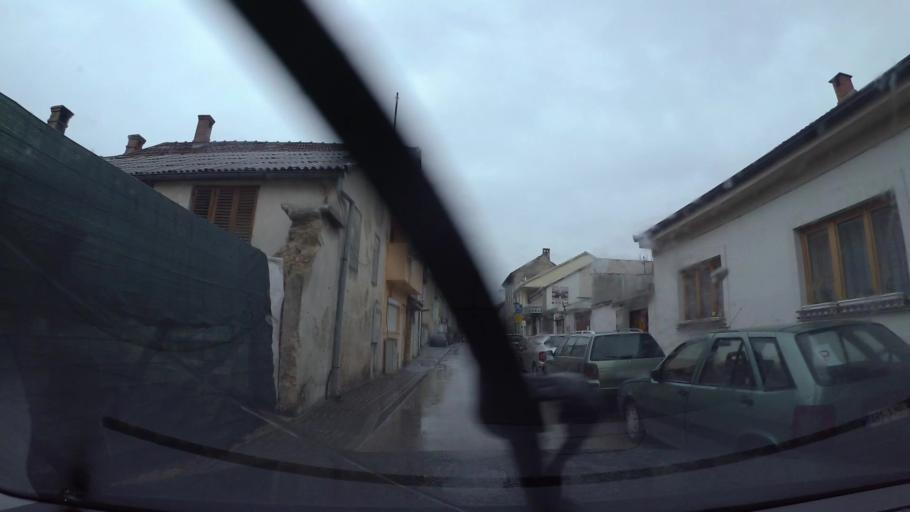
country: BA
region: Federation of Bosnia and Herzegovina
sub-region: Hercegovacko-Bosanski Kanton
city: Mostar
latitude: 43.3464
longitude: 17.8125
